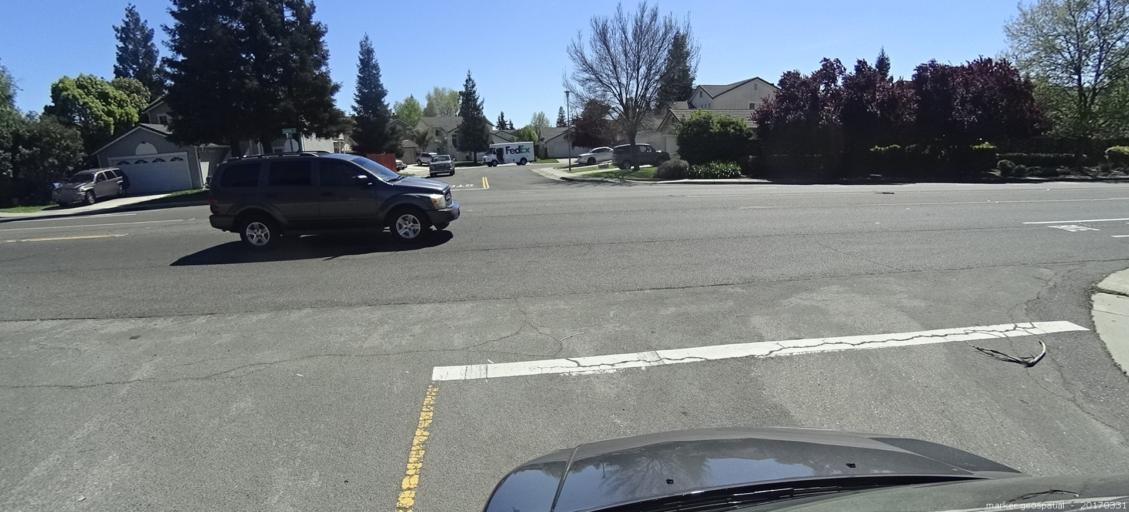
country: US
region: California
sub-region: Sacramento County
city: Laguna
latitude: 38.4490
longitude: -121.4428
